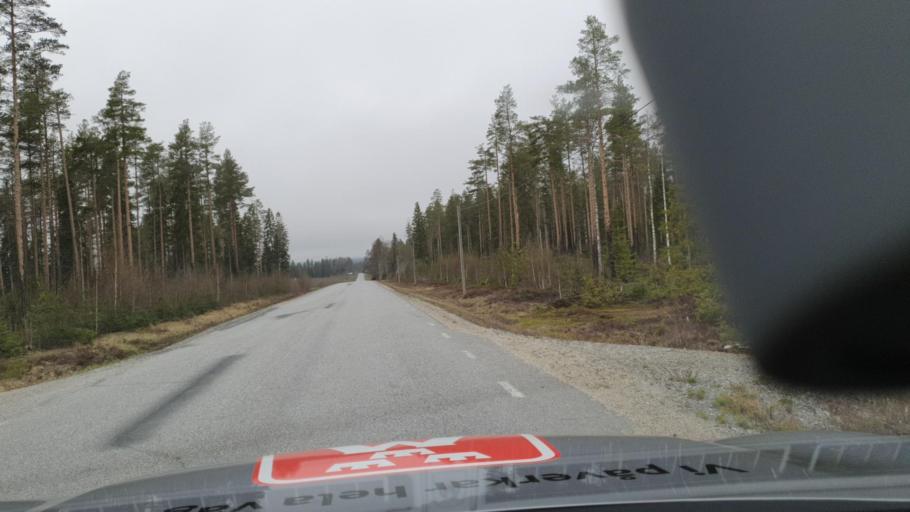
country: SE
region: Vaesternorrland
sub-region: OErnskoeldsviks Kommun
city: Husum
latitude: 63.5466
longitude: 19.0748
